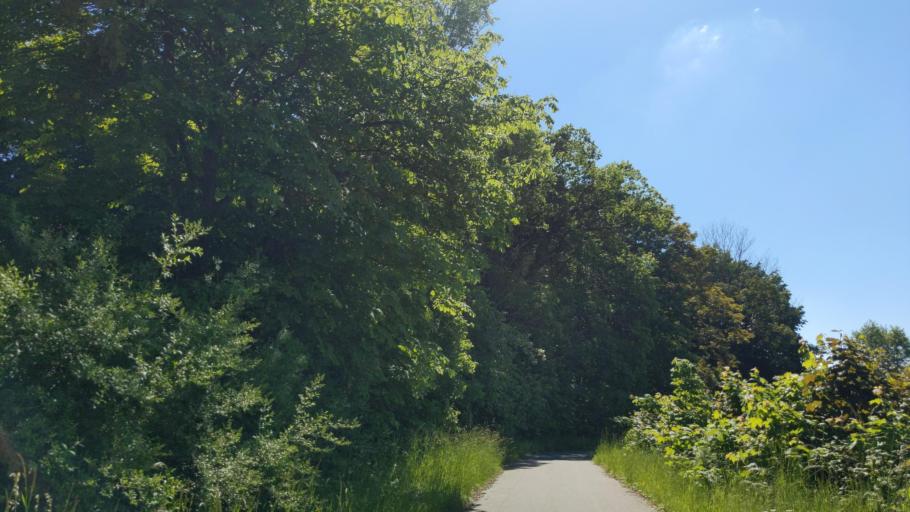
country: DE
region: Schleswig-Holstein
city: Eutin
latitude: 54.1360
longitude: 10.6392
